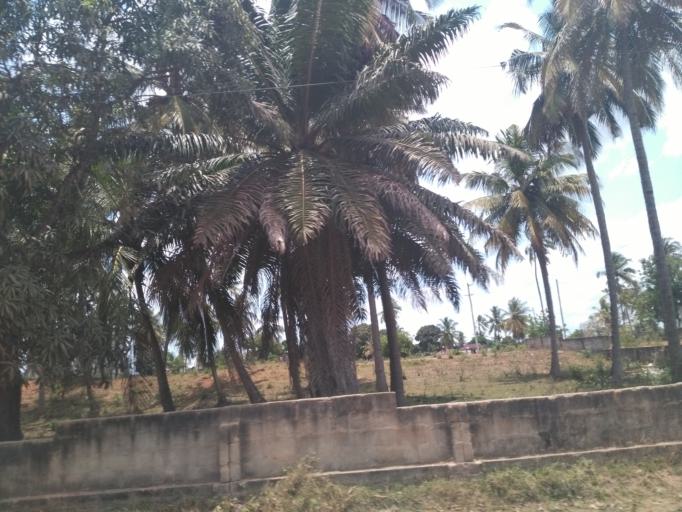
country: TZ
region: Dar es Salaam
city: Dar es Salaam
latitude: -6.8401
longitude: 39.3302
